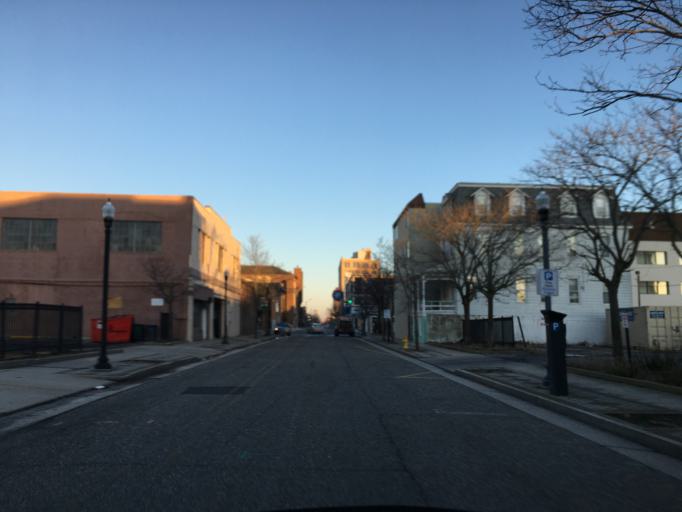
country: US
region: New Jersey
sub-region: Atlantic County
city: Atlantic City
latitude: 39.3594
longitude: -74.4278
